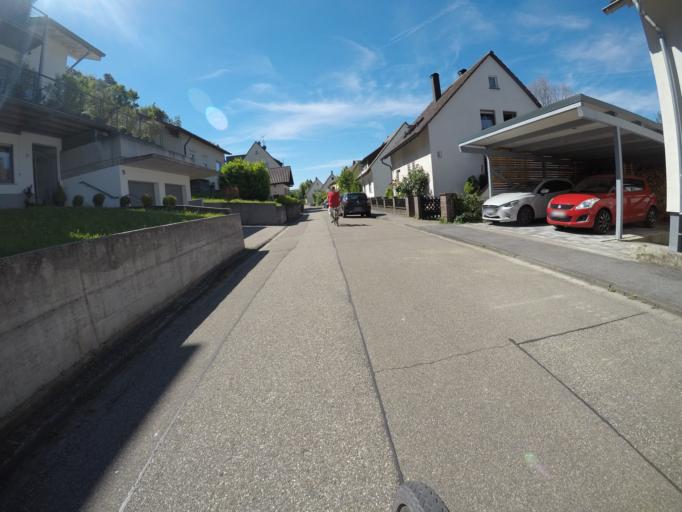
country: DE
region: Baden-Wuerttemberg
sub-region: Karlsruhe Region
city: Konigsbach-Stein
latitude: 48.9461
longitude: 8.6271
